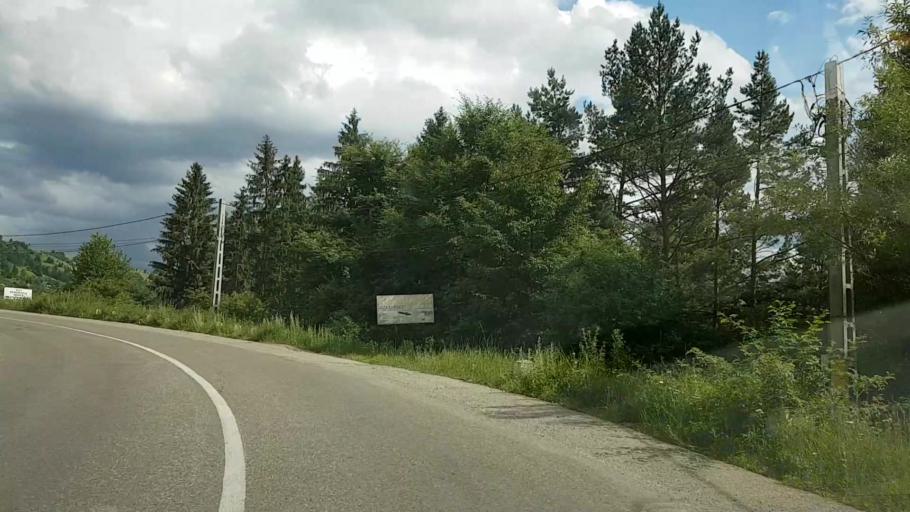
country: RO
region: Neamt
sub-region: Comuna Hangu
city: Hangu
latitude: 47.0103
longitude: 26.0848
